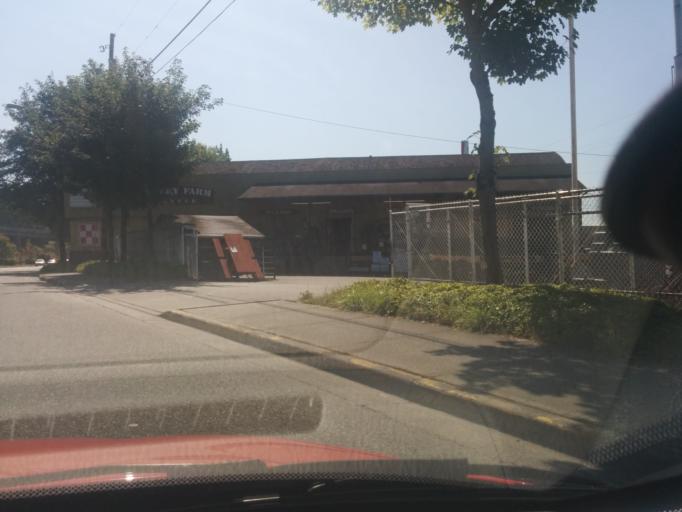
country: US
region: Washington
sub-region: Skagit County
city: Mount Vernon
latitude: 48.4238
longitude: -122.3377
